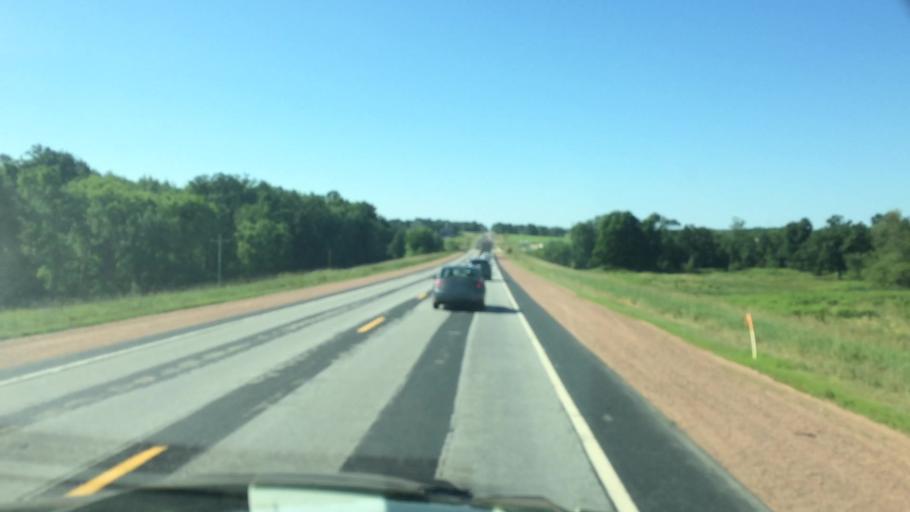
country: US
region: Wisconsin
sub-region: Marathon County
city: Stratford
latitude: 44.8248
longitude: -90.0792
